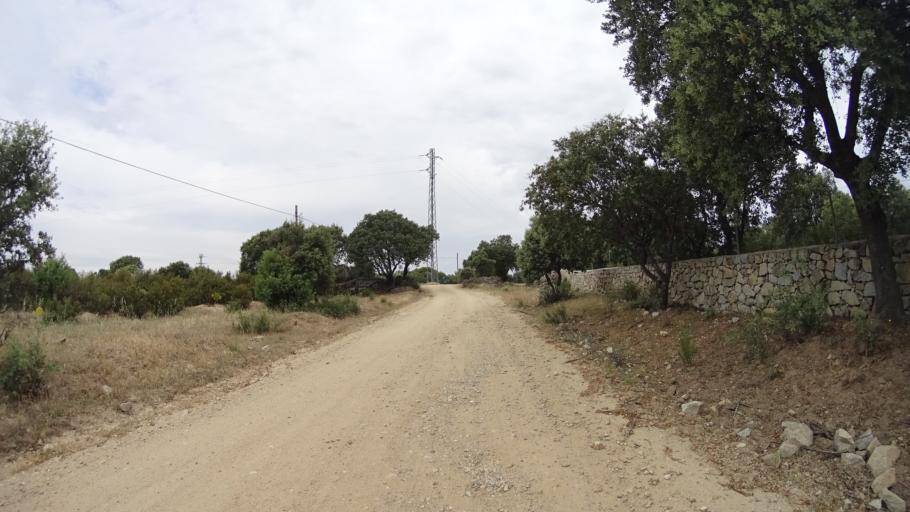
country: ES
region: Madrid
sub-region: Provincia de Madrid
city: Colmenarejo
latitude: 40.5467
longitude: -4.0384
